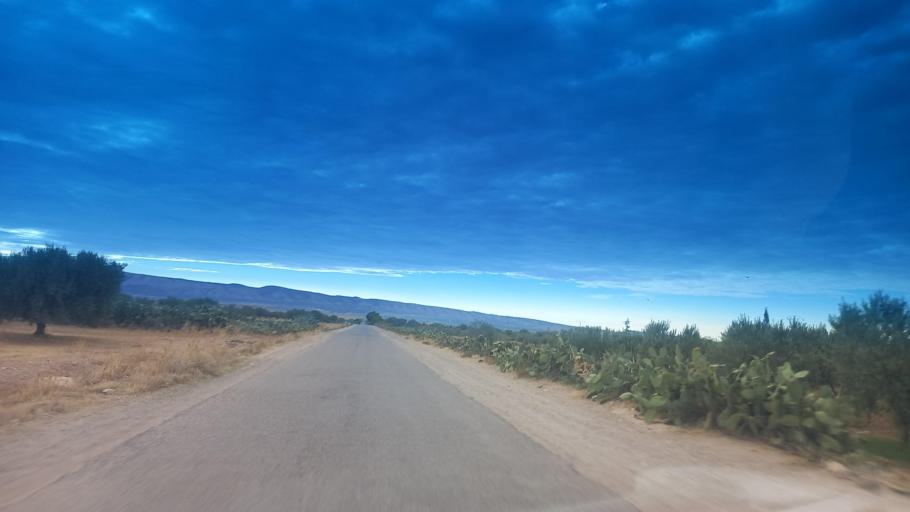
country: TN
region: Al Qasrayn
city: Sbiba
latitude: 35.3736
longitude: 9.0698
